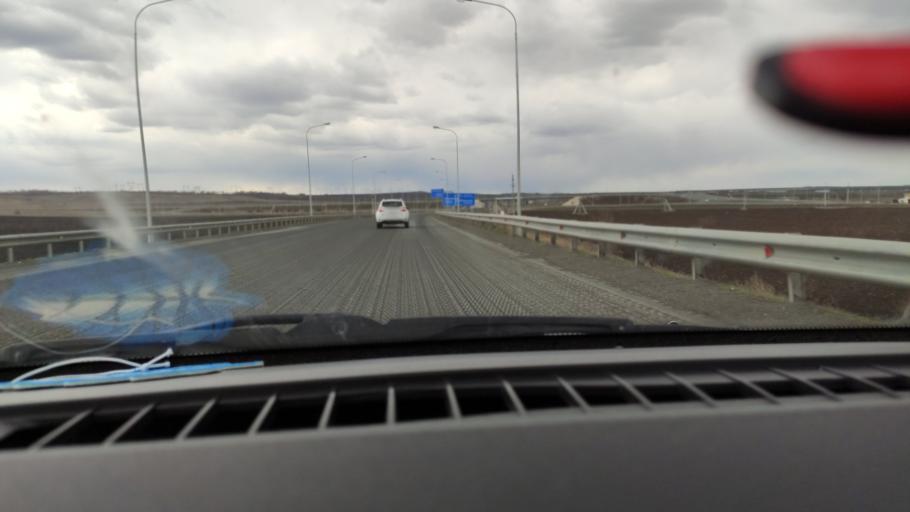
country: RU
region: Saratov
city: Yelshanka
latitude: 51.7973
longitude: 46.1796
